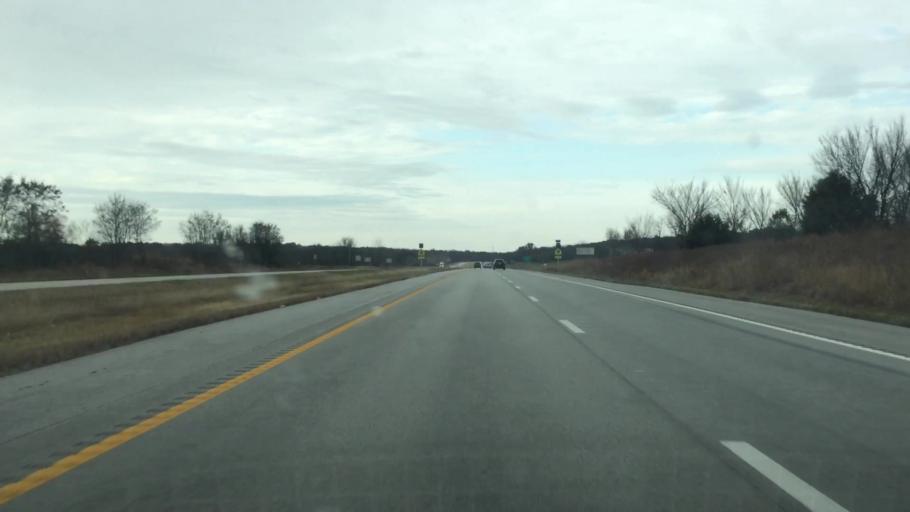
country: US
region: Missouri
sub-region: Saint Clair County
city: Osceola
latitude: 38.2035
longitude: -93.7507
